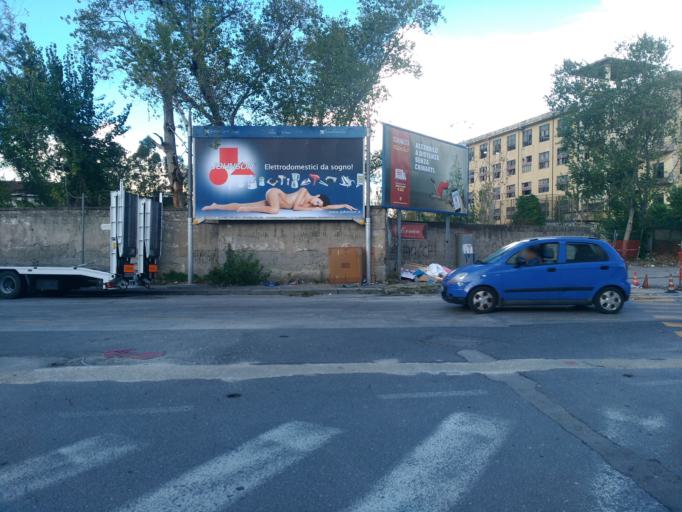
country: IT
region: Campania
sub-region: Provincia di Napoli
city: Napoli
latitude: 40.8489
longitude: 14.2921
